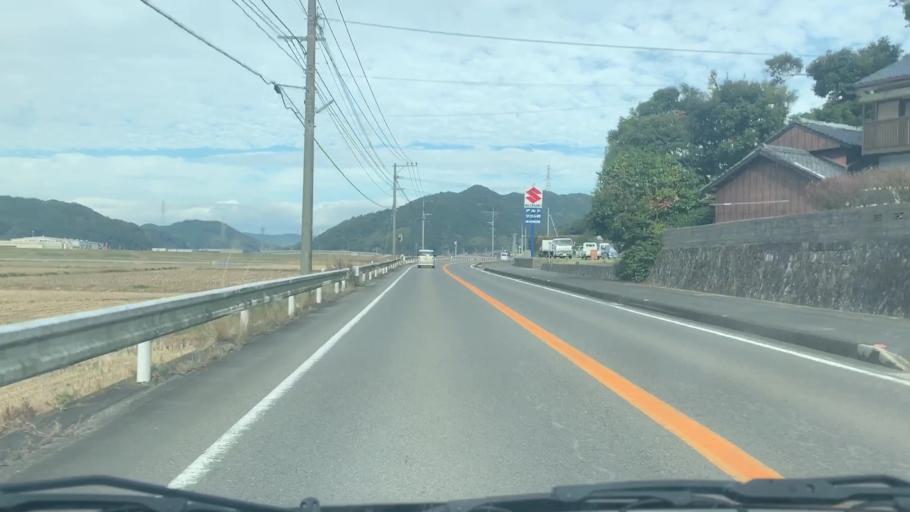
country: JP
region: Saga Prefecture
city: Karatsu
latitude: 33.3682
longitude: 130.0047
